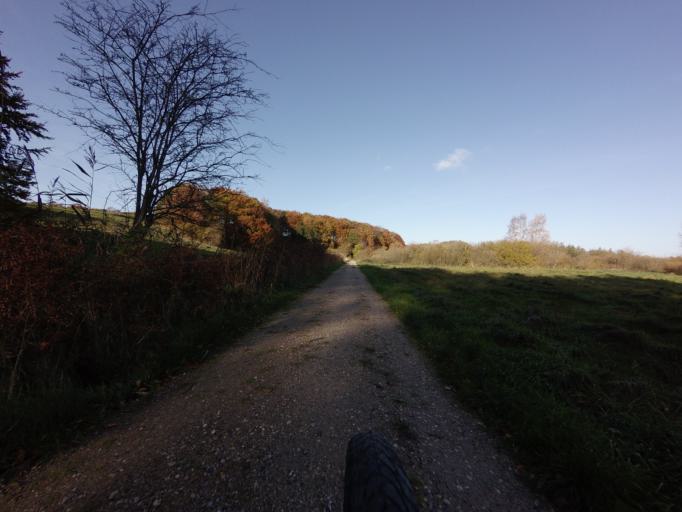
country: DK
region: Central Jutland
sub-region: Syddjurs Kommune
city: Ryomgard
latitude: 56.4440
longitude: 10.6215
